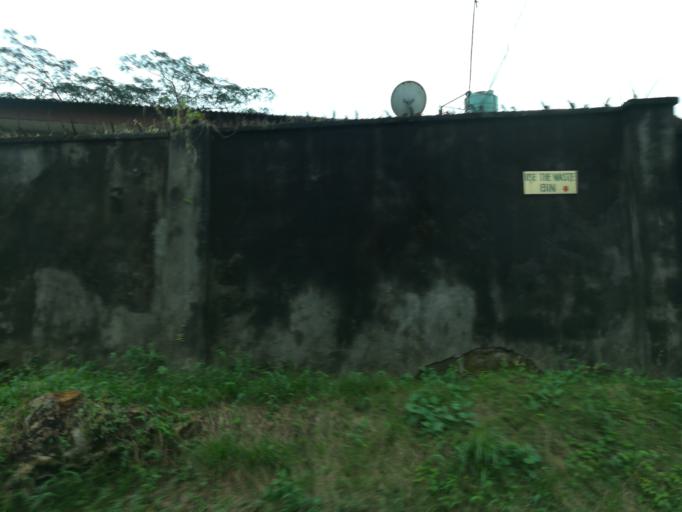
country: NG
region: Rivers
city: Port Harcourt
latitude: 4.8450
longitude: 7.0332
